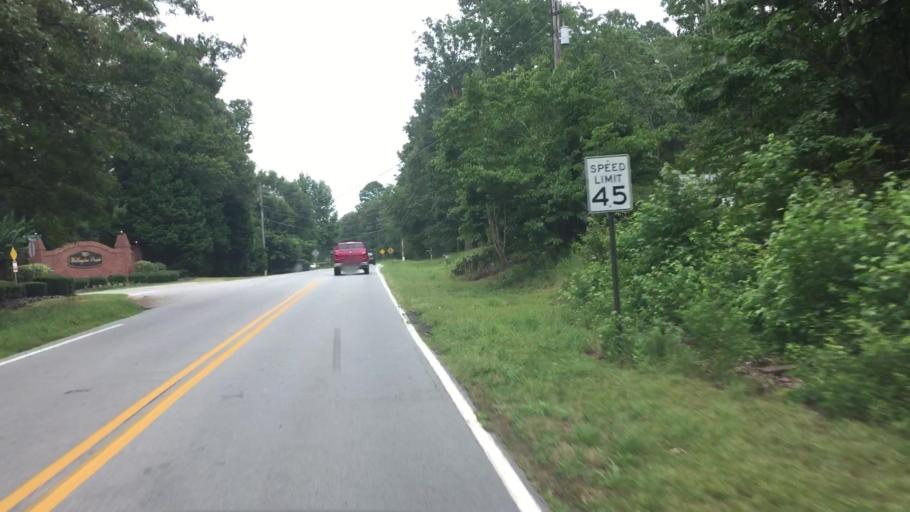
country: US
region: Georgia
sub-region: Barrow County
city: Winder
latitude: 34.0286
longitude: -83.7360
